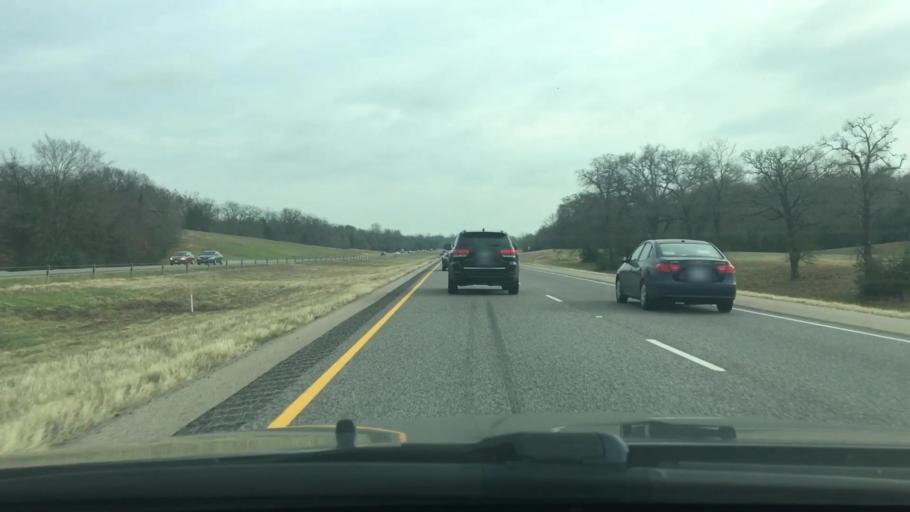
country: US
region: Texas
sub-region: Leon County
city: Buffalo
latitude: 31.5091
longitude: -96.1023
